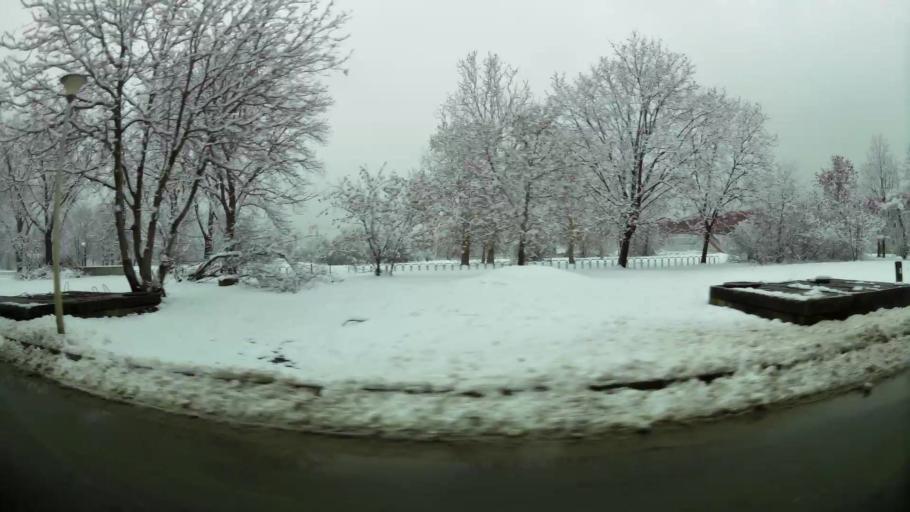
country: RS
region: Central Serbia
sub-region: Belgrade
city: Novi Beograd
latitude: 44.8050
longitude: 20.4392
